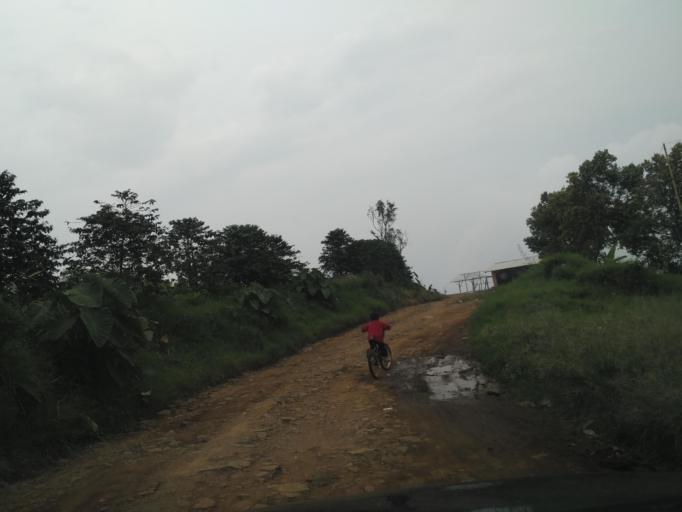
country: ID
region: West Java
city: Caringin
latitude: -6.6762
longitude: 107.0256
